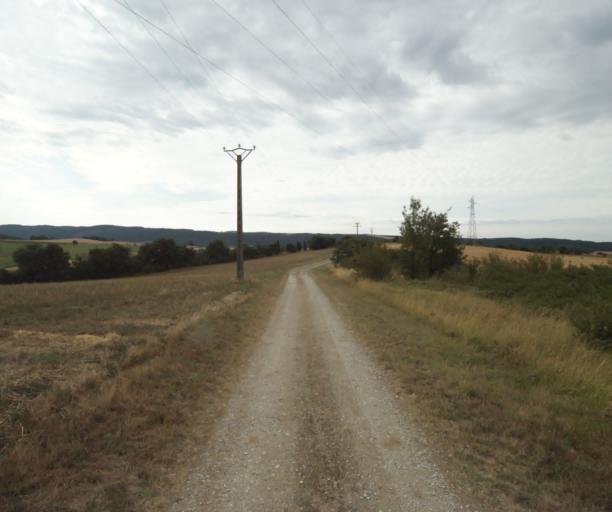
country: FR
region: Midi-Pyrenees
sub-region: Departement de la Haute-Garonne
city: Revel
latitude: 43.4326
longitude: 1.9650
